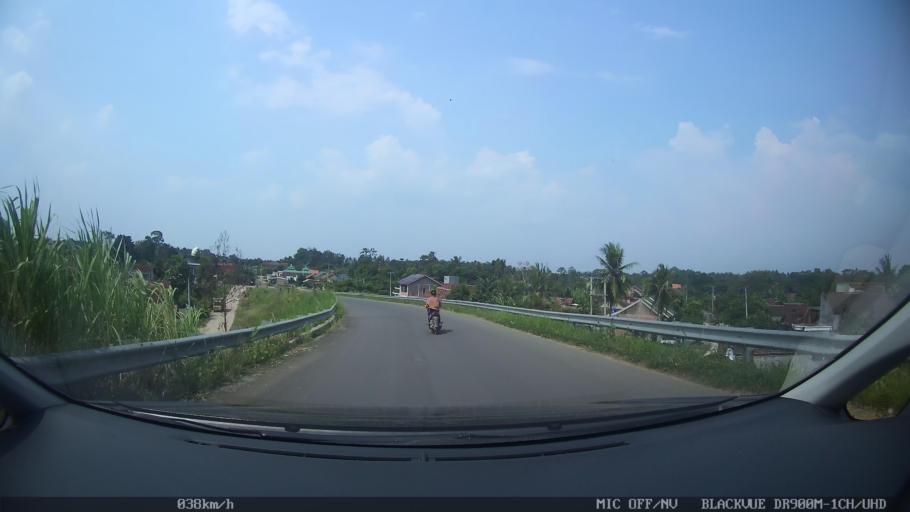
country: ID
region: Lampung
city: Natar
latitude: -5.3011
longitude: 105.2422
